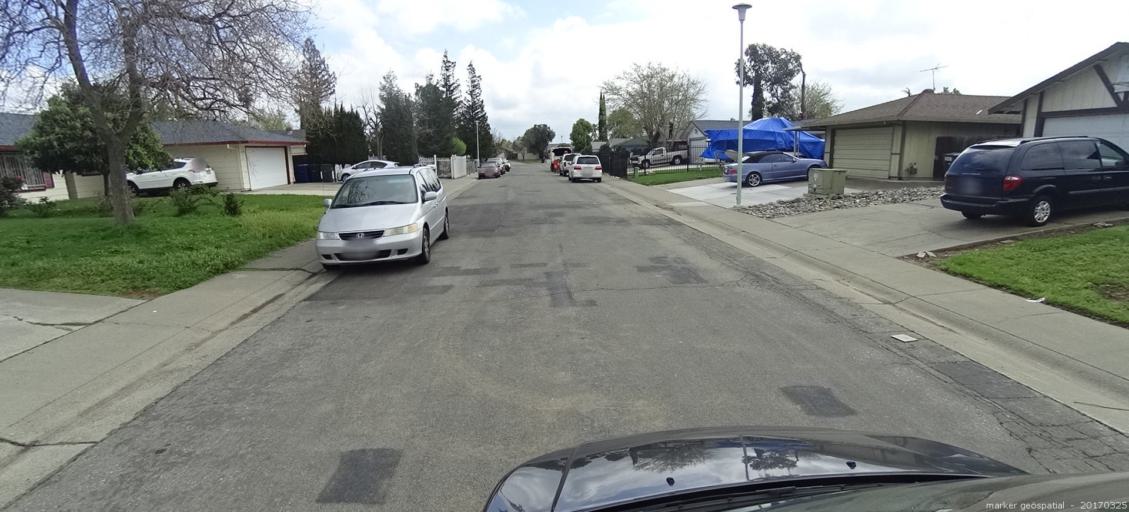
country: US
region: California
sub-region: Sacramento County
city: Florin
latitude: 38.5175
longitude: -121.4270
